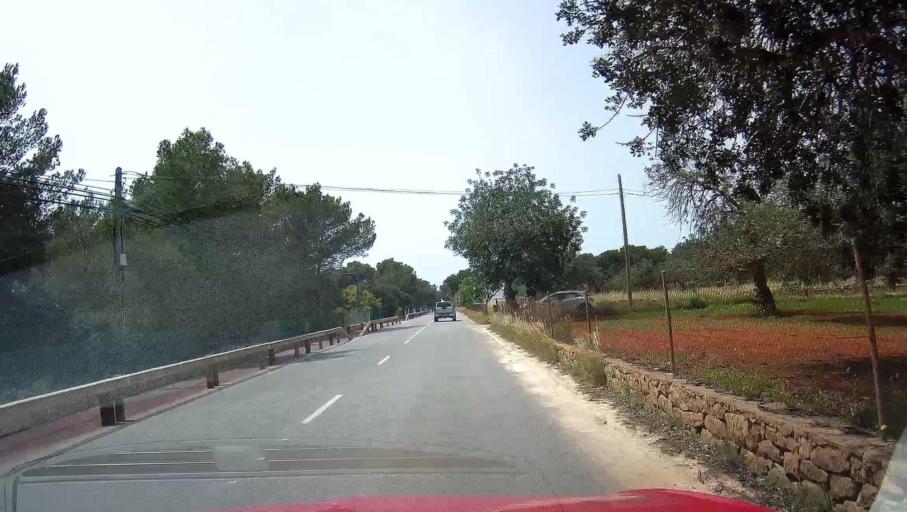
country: ES
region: Balearic Islands
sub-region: Illes Balears
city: Santa Eularia des Riu
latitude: 39.0016
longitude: 1.5652
